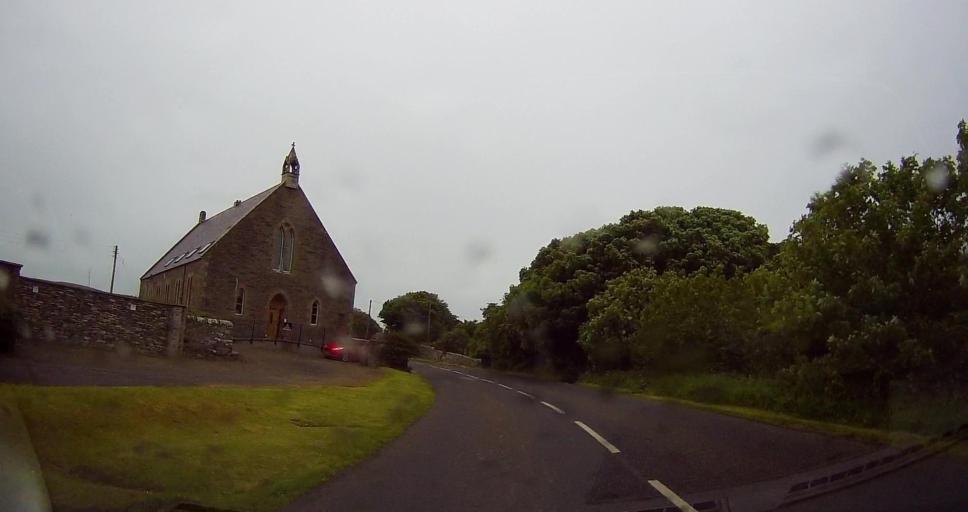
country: GB
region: Scotland
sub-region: Orkney Islands
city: Orkney
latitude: 59.1126
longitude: -3.1050
